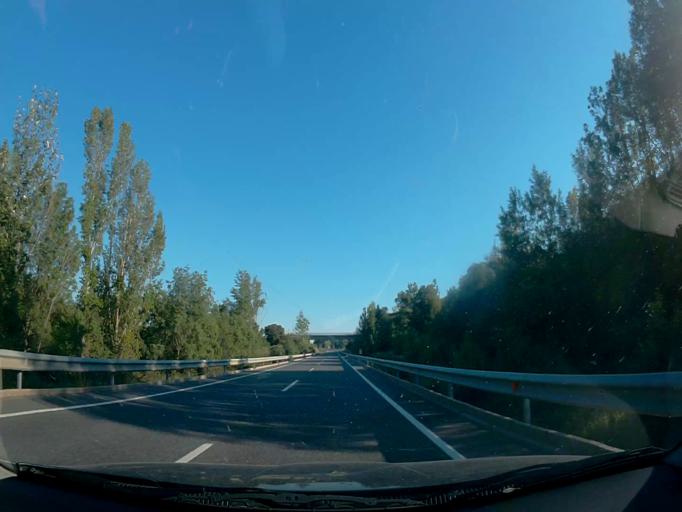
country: ES
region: Castille-La Mancha
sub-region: Province of Toledo
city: Escalona
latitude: 40.1742
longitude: -4.3995
